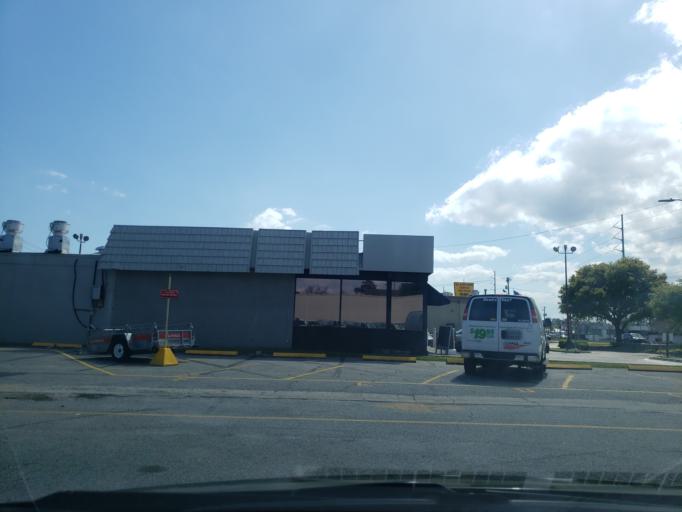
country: US
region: Georgia
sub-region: Chatham County
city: Montgomery
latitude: 31.9971
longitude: -81.1276
